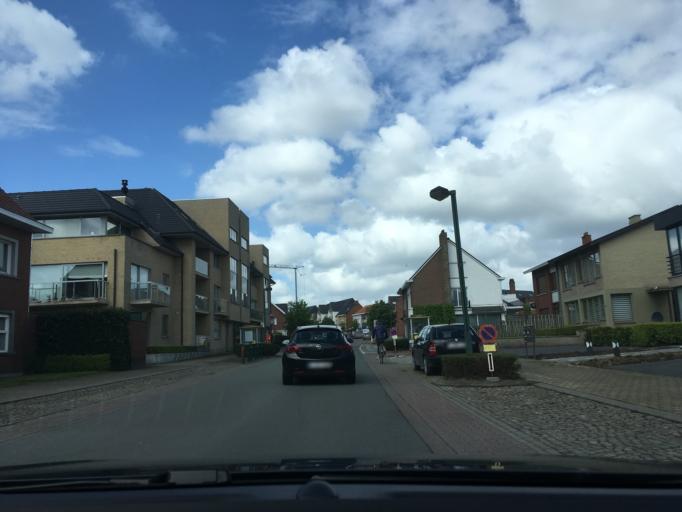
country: BE
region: Flanders
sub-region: Provincie West-Vlaanderen
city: Pittem
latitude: 50.9930
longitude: 3.2707
